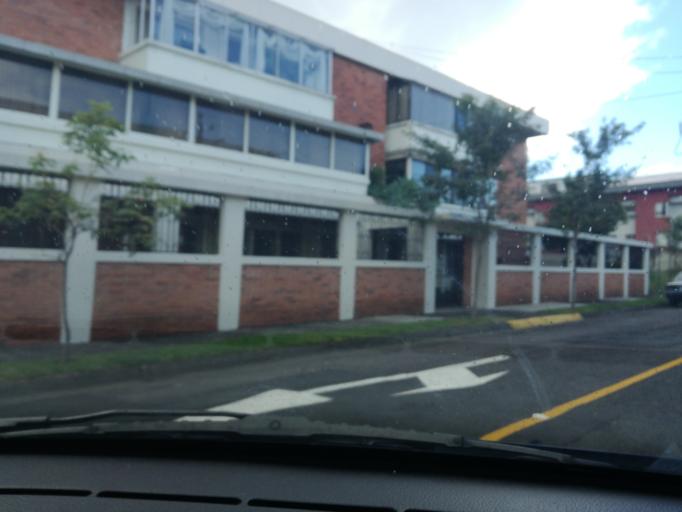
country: CR
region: San Jose
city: San Pedro
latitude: 9.9241
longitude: -84.0441
